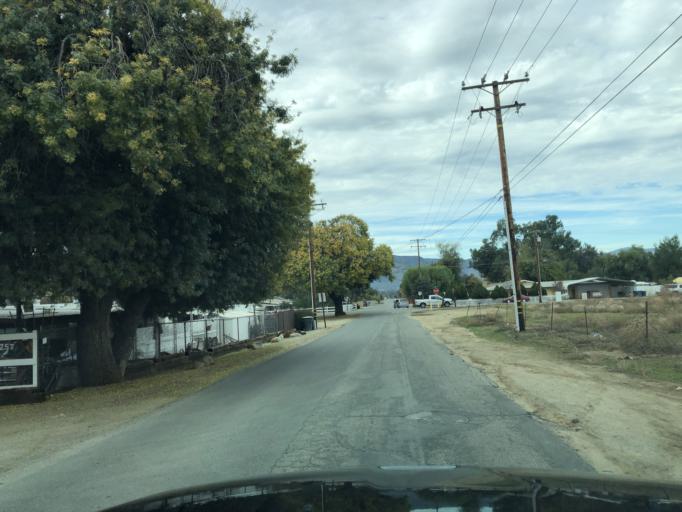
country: US
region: California
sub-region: Riverside County
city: Sedco Hills
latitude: 33.6233
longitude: -117.2744
